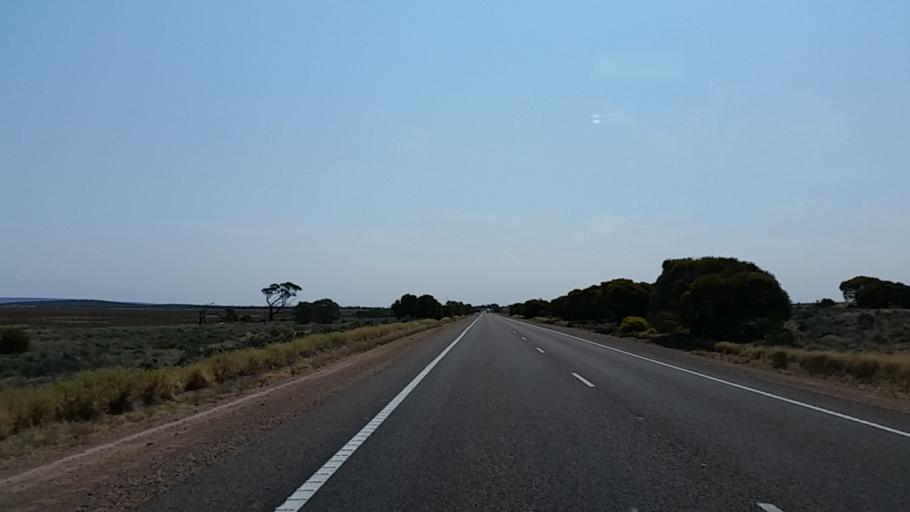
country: AU
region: South Australia
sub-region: Port Augusta
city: Port Augusta
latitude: -32.7578
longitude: 137.9501
